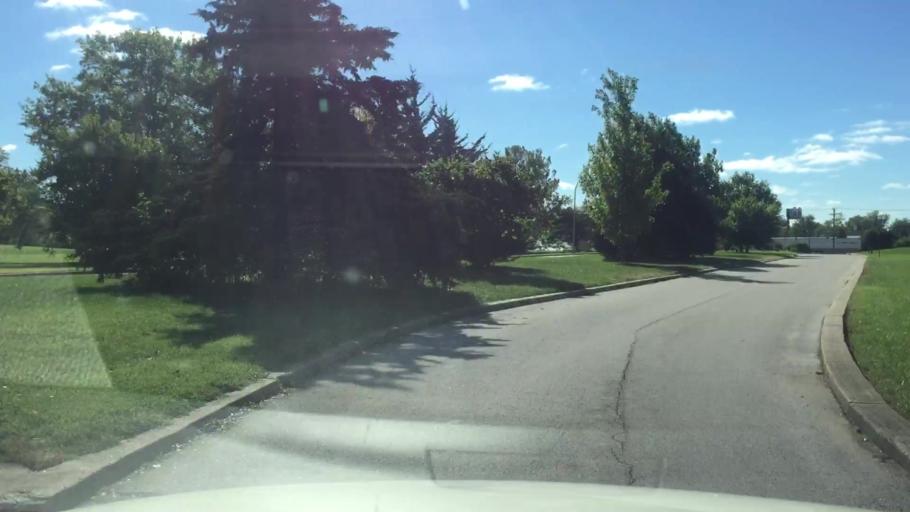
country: US
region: Missouri
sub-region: Boone County
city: Columbia
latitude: 38.9696
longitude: -92.3634
